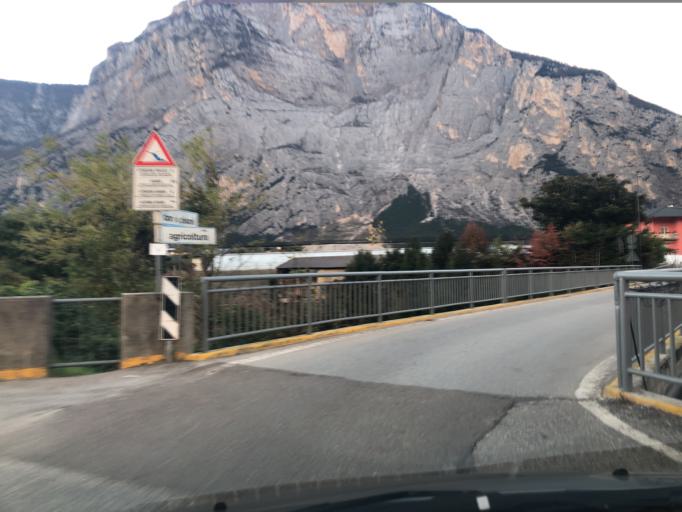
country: IT
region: Trentino-Alto Adige
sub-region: Provincia di Trento
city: Pietramurata
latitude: 46.0266
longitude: 10.9594
